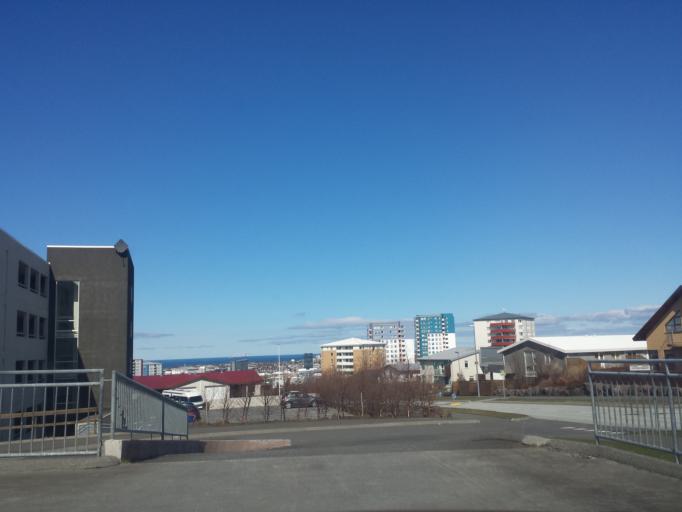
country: IS
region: Capital Region
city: Reykjavik
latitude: 64.0923
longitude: -21.8478
